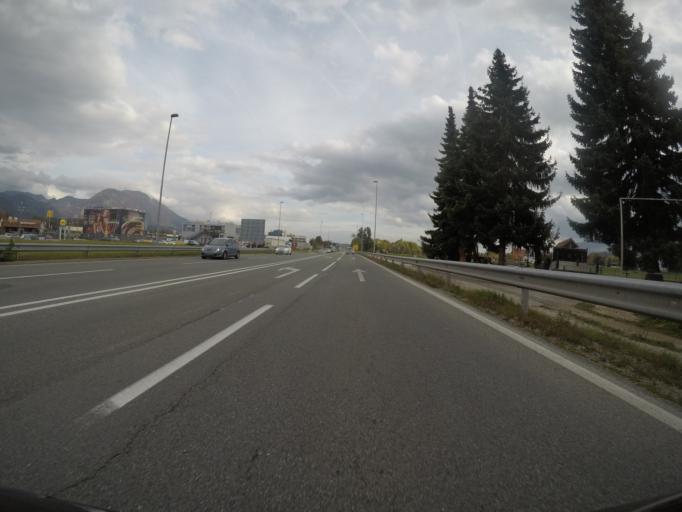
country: SI
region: Radovljica
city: Lesce
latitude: 46.3658
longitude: 14.1579
